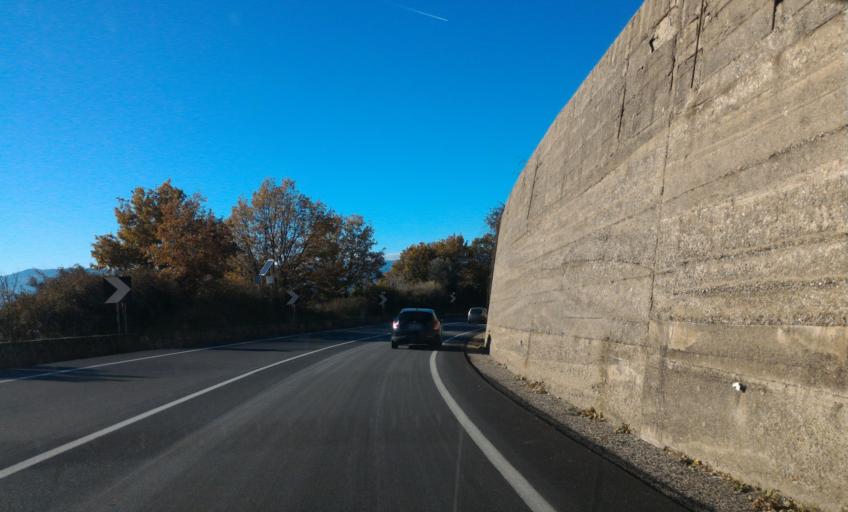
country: IT
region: Calabria
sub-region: Provincia di Cosenza
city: Rovito
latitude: 39.3050
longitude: 16.3226
